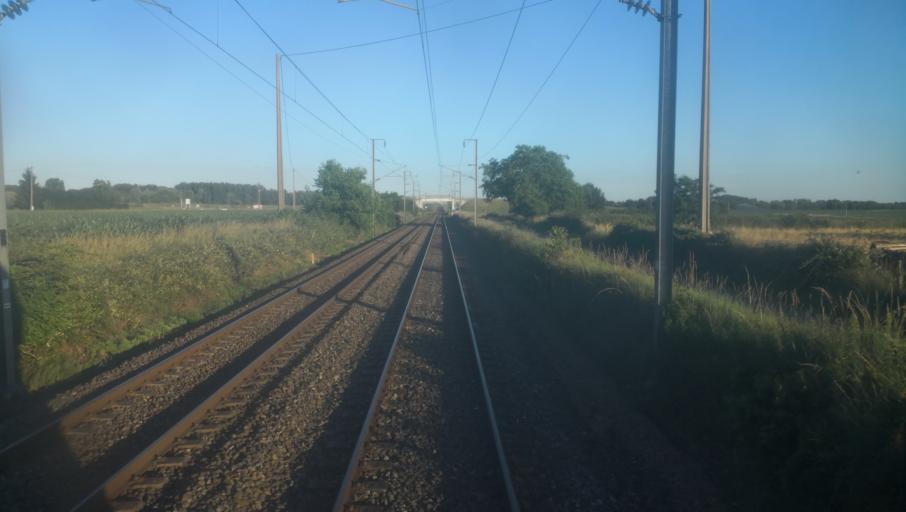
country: FR
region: Auvergne
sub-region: Departement de l'Allier
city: Trevol
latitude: 46.6463
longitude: 3.2686
